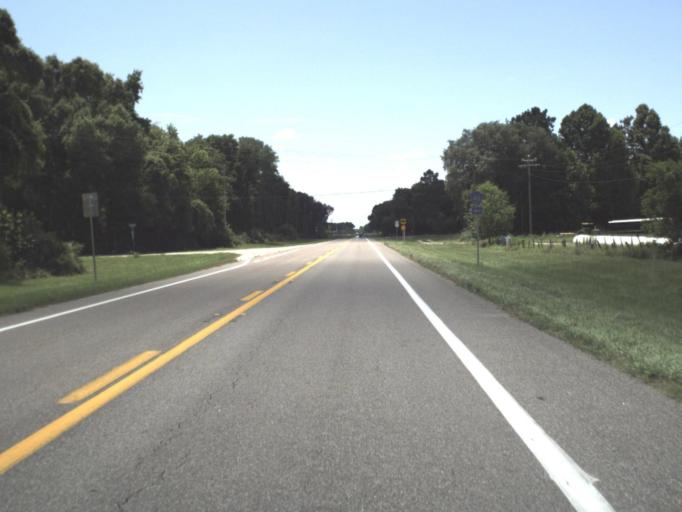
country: US
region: Florida
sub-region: Lafayette County
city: Mayo
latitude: 30.0318
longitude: -83.0614
